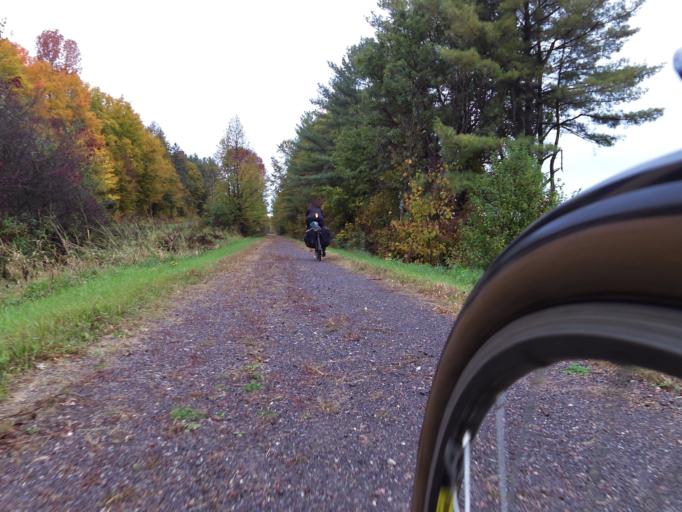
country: CA
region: Quebec
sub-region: Outaouais
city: Shawville
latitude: 45.6933
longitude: -76.5718
